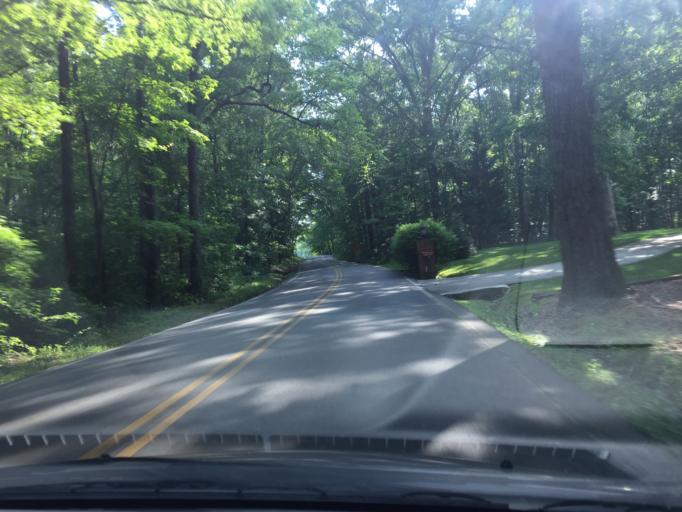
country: US
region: Tennessee
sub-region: Hamilton County
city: Collegedale
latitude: 35.0696
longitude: -85.0073
